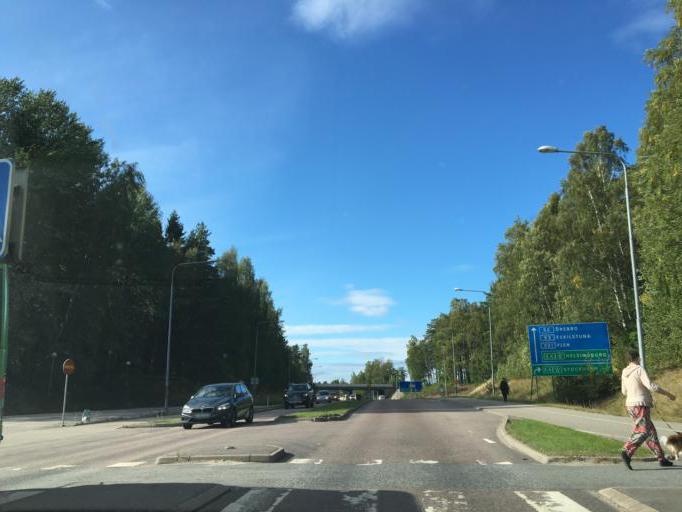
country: SE
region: Soedermanland
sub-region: Nykopings Kommun
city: Nykoping
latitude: 58.7625
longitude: 16.9940
